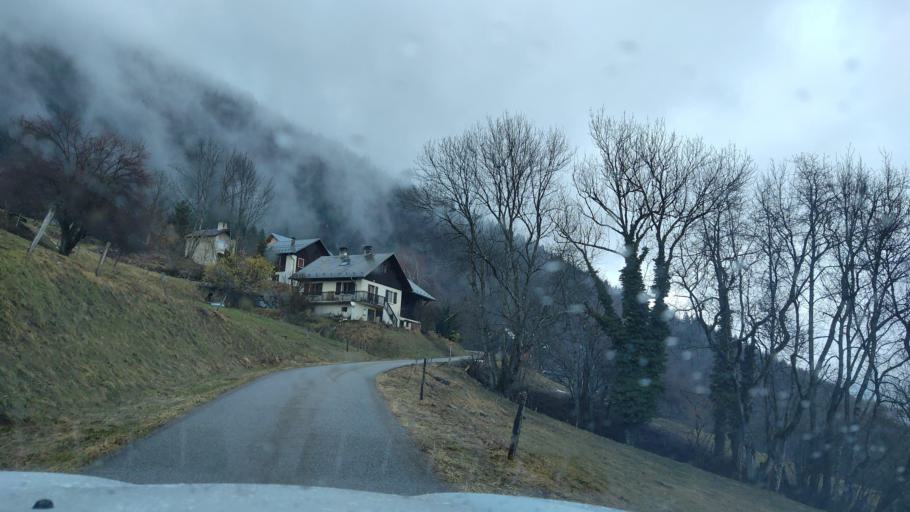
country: FR
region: Rhone-Alpes
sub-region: Departement de la Savoie
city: Aiton
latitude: 45.5092
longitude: 6.2797
